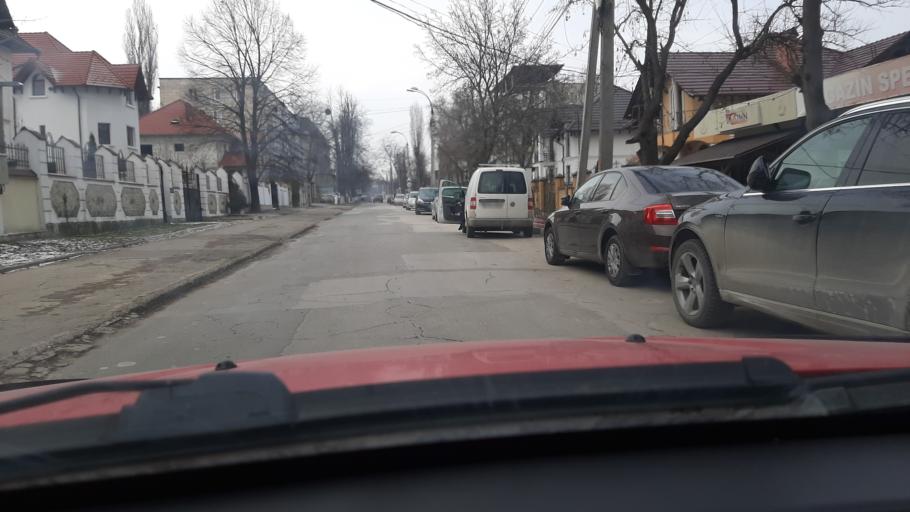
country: MD
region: Chisinau
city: Vatra
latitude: 47.0317
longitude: 28.7889
